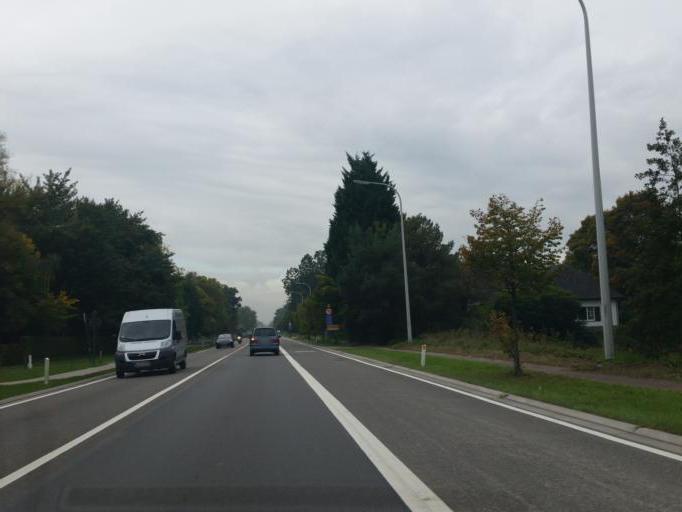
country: BE
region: Flanders
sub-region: Provincie Vlaams-Brabant
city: Steenokkerzeel
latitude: 50.9273
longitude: 4.5228
